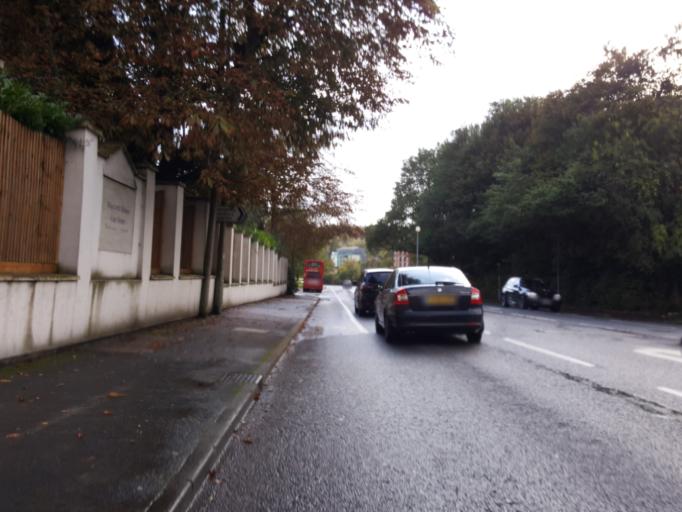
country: GB
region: England
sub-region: Brighton and Hove
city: Hove
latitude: 50.8564
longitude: -0.1538
